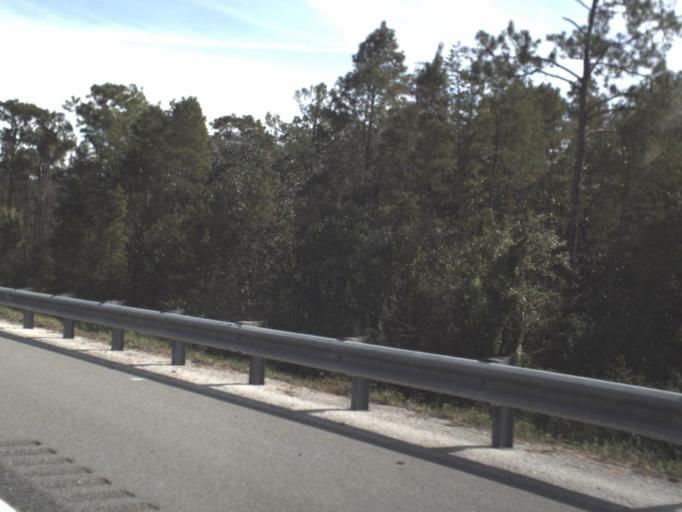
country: US
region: Florida
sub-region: Osceola County
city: Celebration
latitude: 28.3490
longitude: -81.4948
